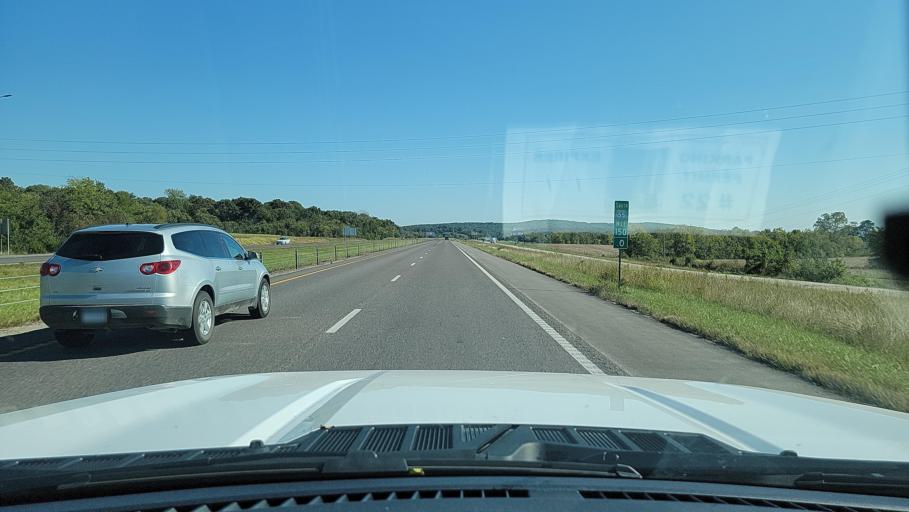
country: US
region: Missouri
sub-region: Sainte Genevieve County
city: Sainte Genevieve
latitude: 37.9337
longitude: -90.1190
